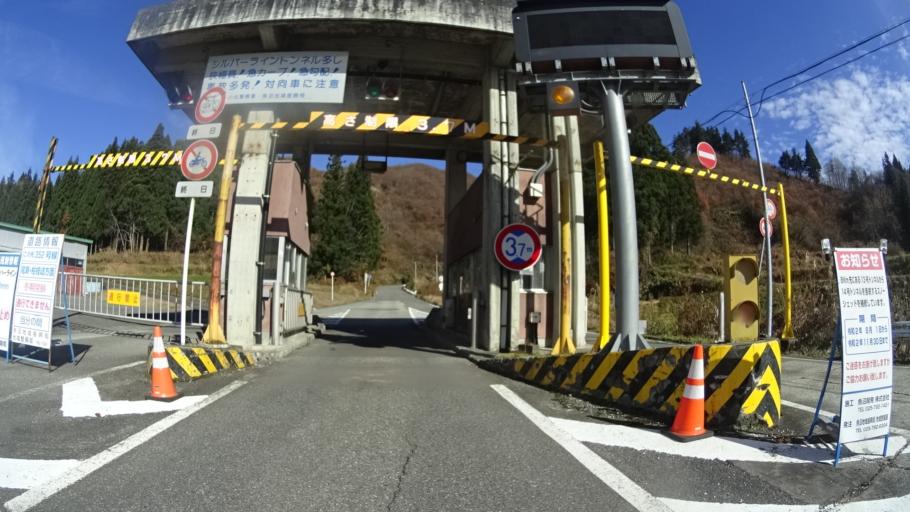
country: JP
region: Niigata
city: Muikamachi
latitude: 37.2049
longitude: 139.0725
